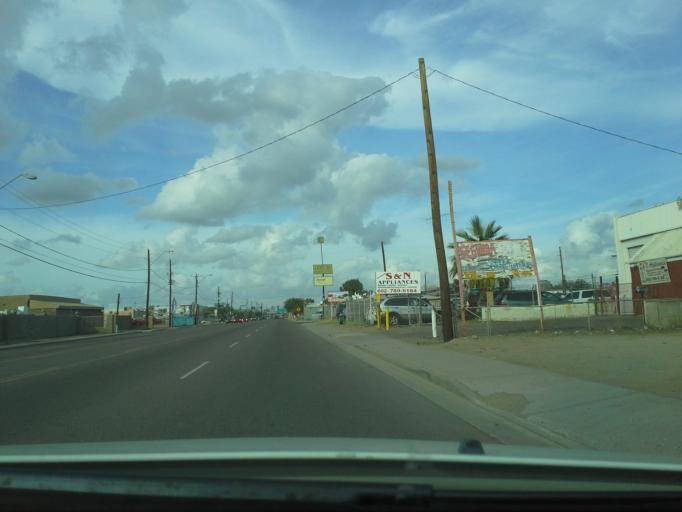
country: US
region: Arizona
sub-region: Maricopa County
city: Phoenix
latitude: 33.4230
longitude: -112.0824
